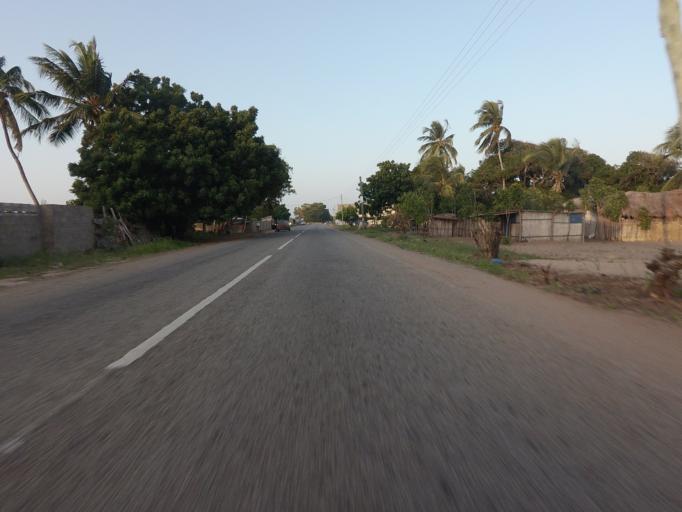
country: GH
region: Volta
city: Anloga
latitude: 5.7880
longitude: 0.8592
